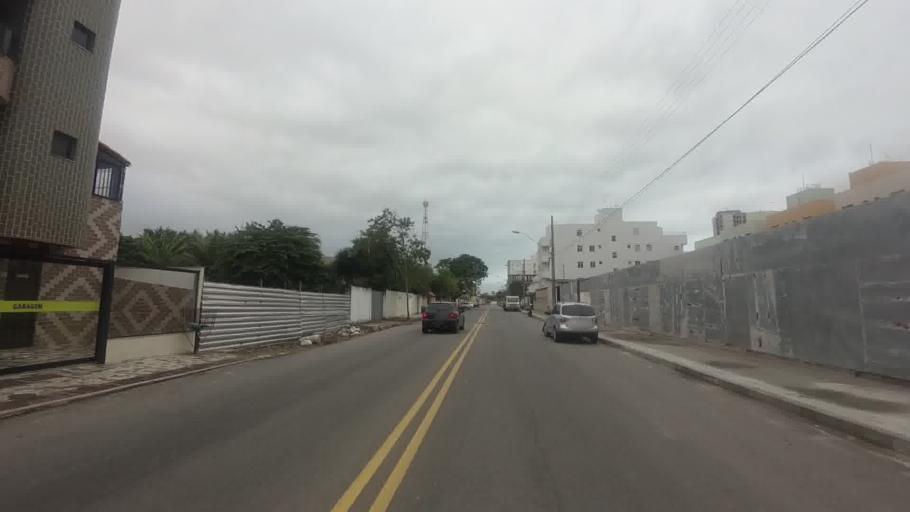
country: BR
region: Espirito Santo
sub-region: Guarapari
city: Guarapari
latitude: -20.6514
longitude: -40.4880
